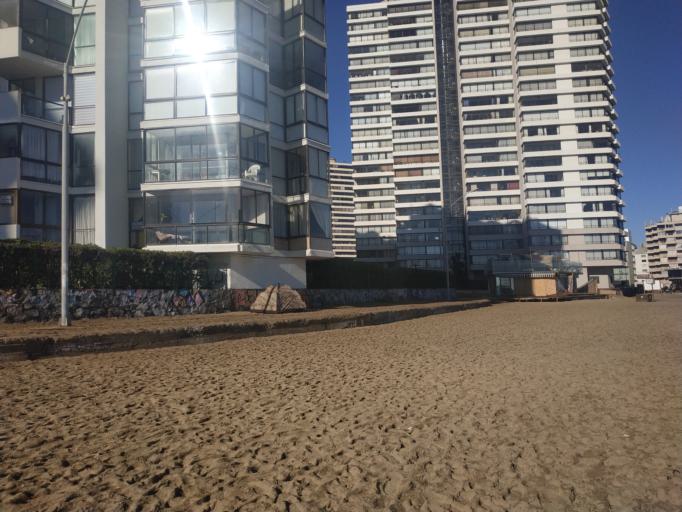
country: CL
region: Valparaiso
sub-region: Provincia de Valparaiso
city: Vina del Mar
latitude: -33.0129
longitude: -71.5548
